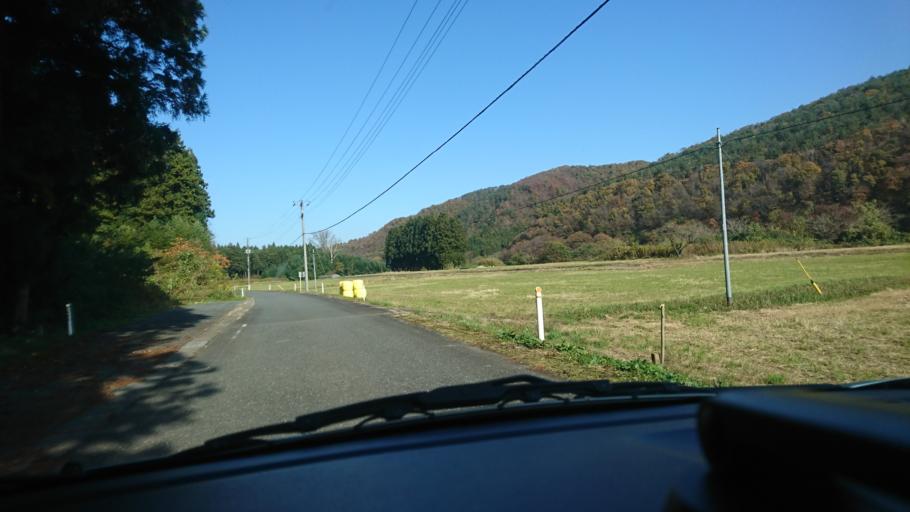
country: JP
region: Iwate
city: Ichinoseki
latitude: 38.8134
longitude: 141.2490
